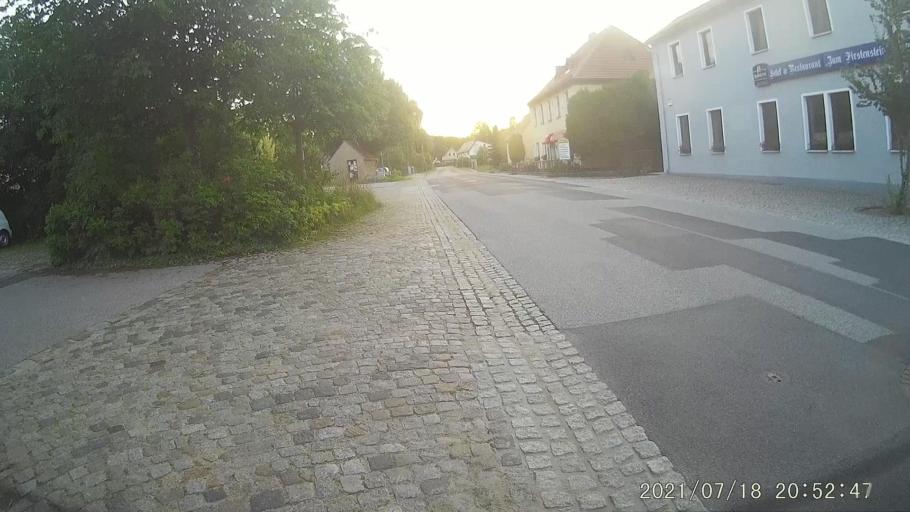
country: DE
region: Saxony
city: Konigshain
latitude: 51.1810
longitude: 14.8668
